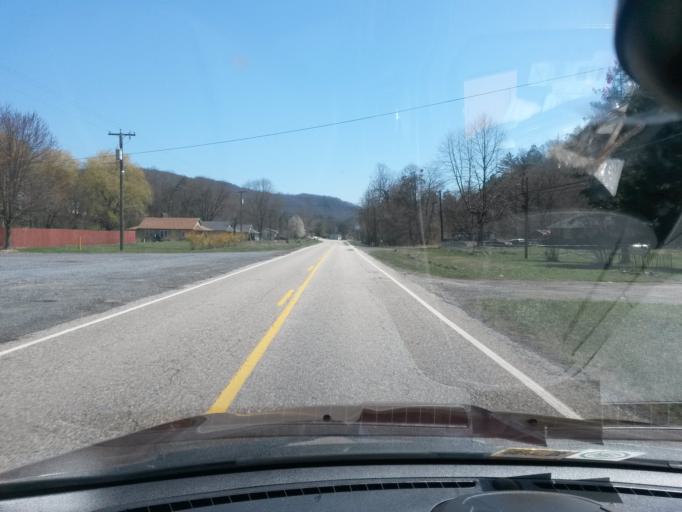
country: US
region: Virginia
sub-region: City of Covington
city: Covington
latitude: 37.8145
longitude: -80.0904
